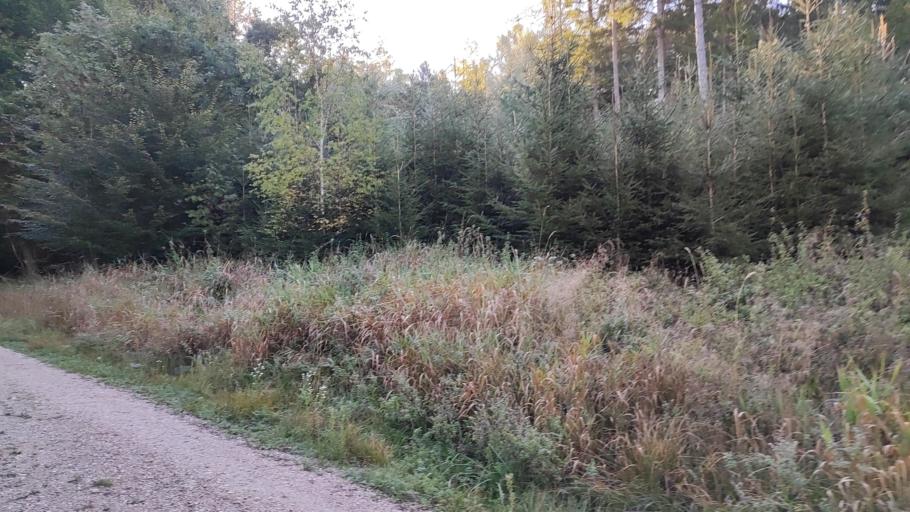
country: DE
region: Bavaria
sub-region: Swabia
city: Welden
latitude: 48.4228
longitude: 10.6368
